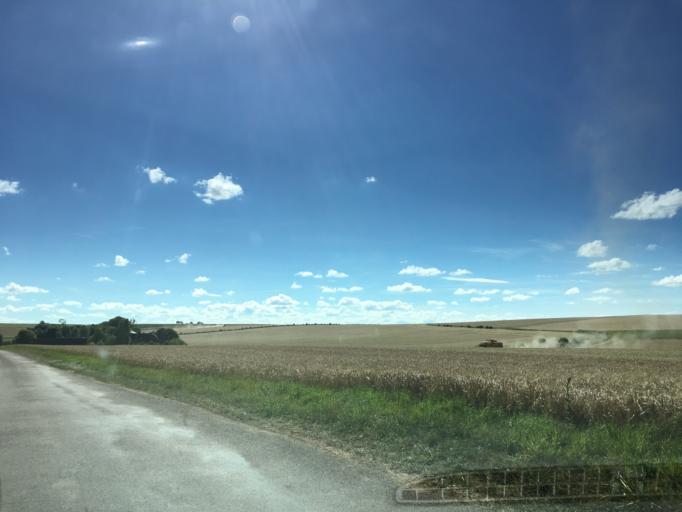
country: FR
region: Bourgogne
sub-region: Departement de l'Yonne
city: Aillant-sur-Tholon
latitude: 47.8672
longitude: 3.3922
